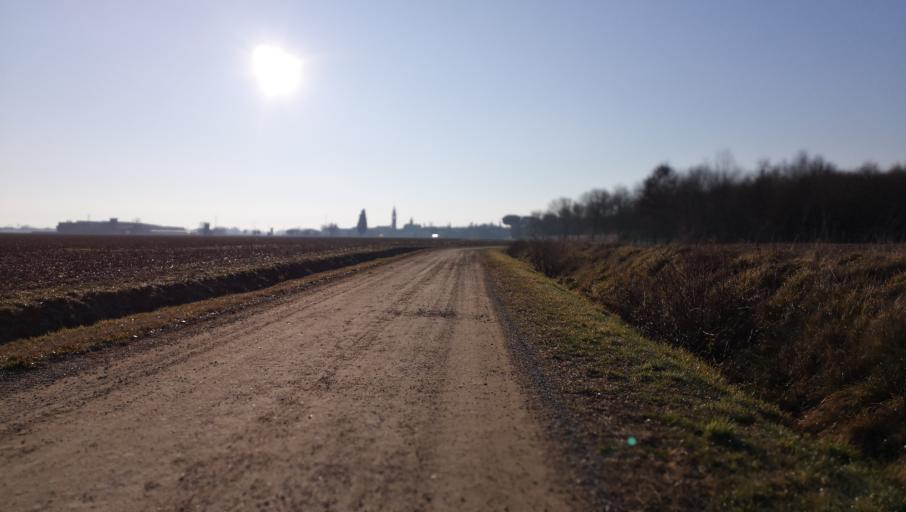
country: IT
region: Friuli Venezia Giulia
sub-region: Provincia di Udine
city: Lauzacco
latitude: 45.9712
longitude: 13.2936
